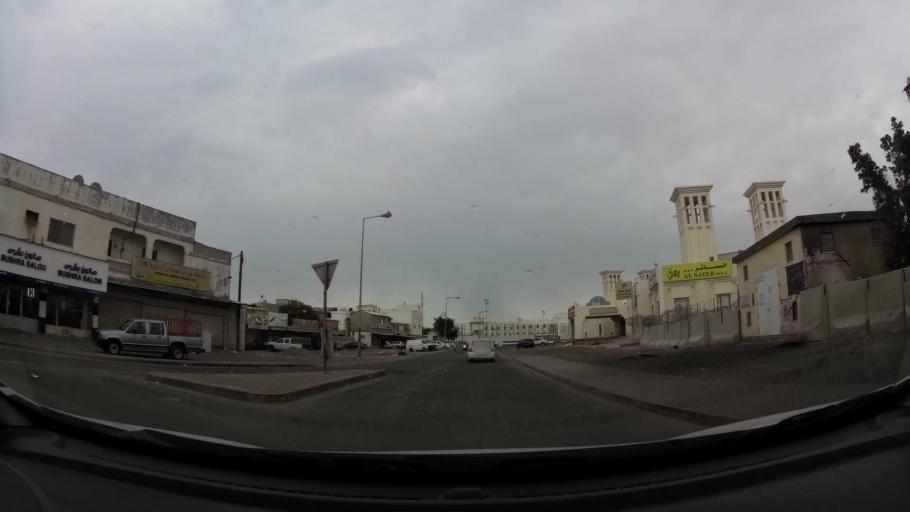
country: BH
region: Central Governorate
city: Madinat Hamad
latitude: 26.1199
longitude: 50.4782
